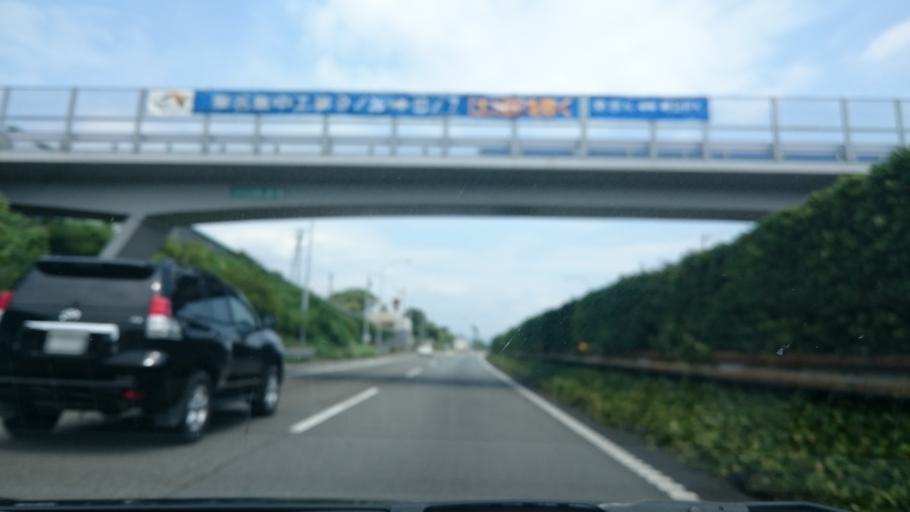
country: JP
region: Shizuoka
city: Shizuoka-shi
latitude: 34.9796
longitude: 138.4320
